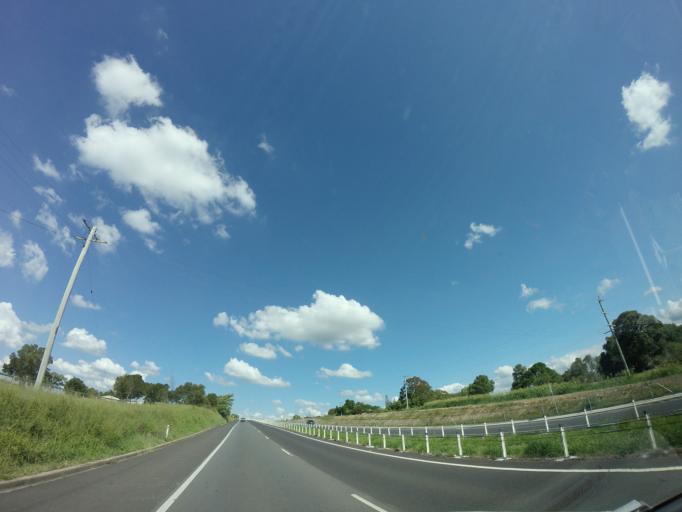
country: AU
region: Queensland
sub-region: Ipswich
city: Thagoona
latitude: -27.5674
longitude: 152.6181
